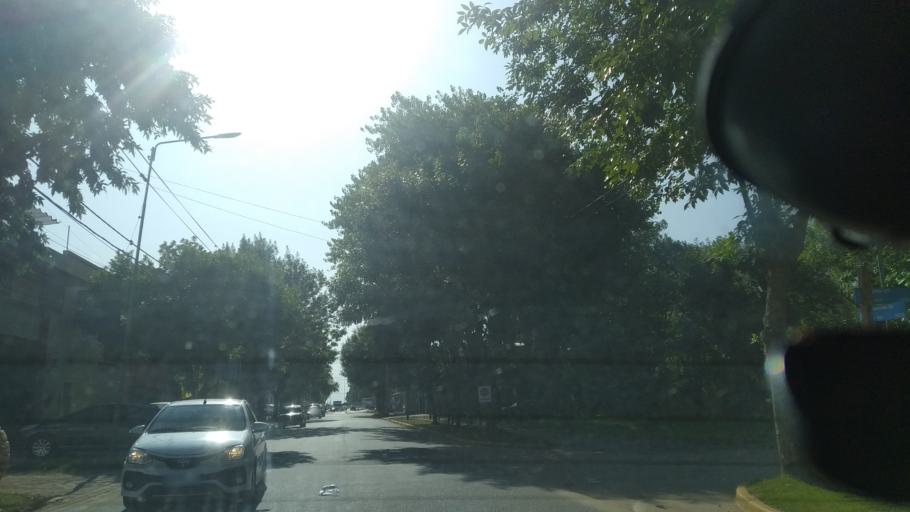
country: AR
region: Buenos Aires
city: Mar del Tuyu
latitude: -36.5335
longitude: -56.7118
